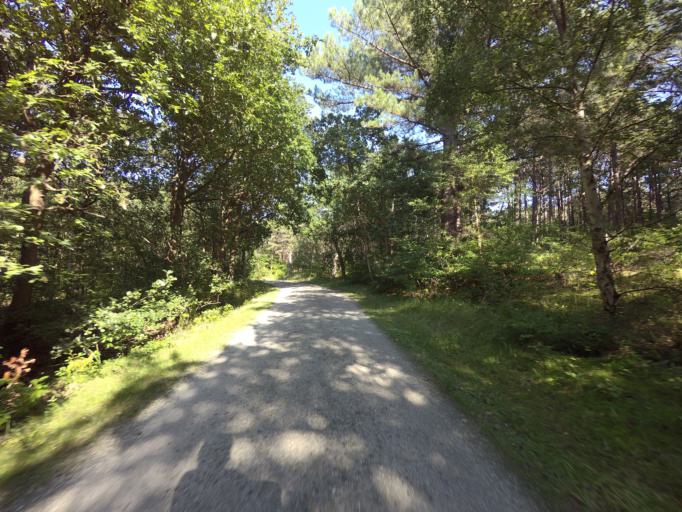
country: NL
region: Friesland
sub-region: Gemeente Terschelling
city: West-Terschelling
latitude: 53.3770
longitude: 5.2369
